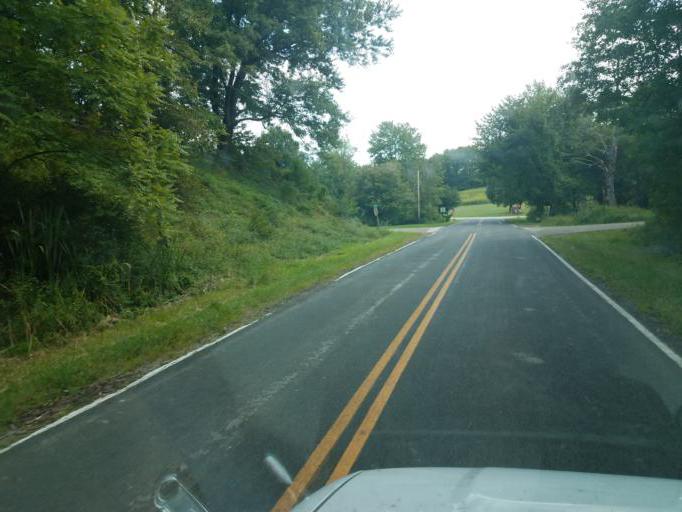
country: US
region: Ohio
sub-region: Stark County
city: East Canton
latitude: 40.7118
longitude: -81.2756
